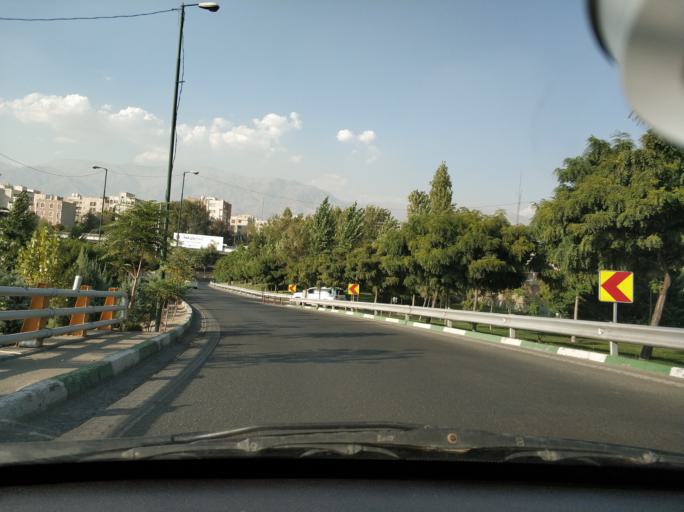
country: IR
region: Tehran
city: Tehran
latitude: 35.7418
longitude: 51.4624
